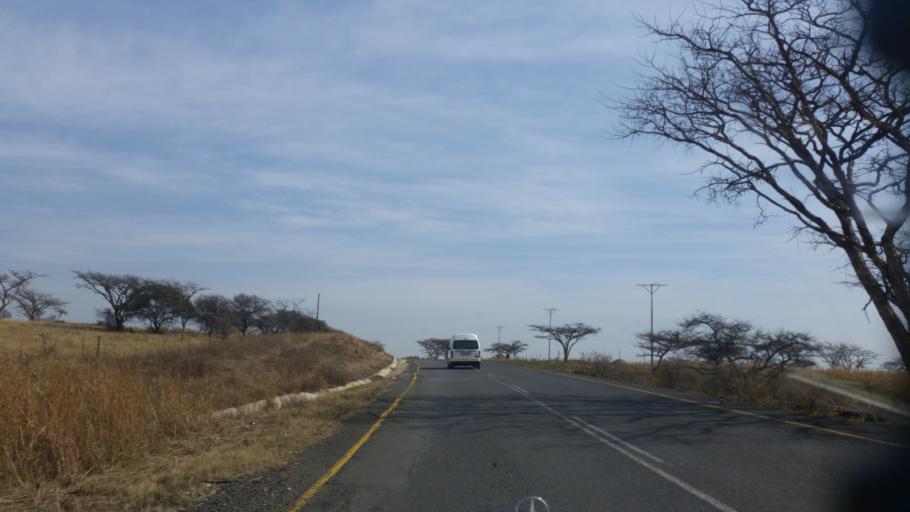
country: ZA
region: KwaZulu-Natal
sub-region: uThukela District Municipality
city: Estcourt
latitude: -29.0573
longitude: 29.9305
